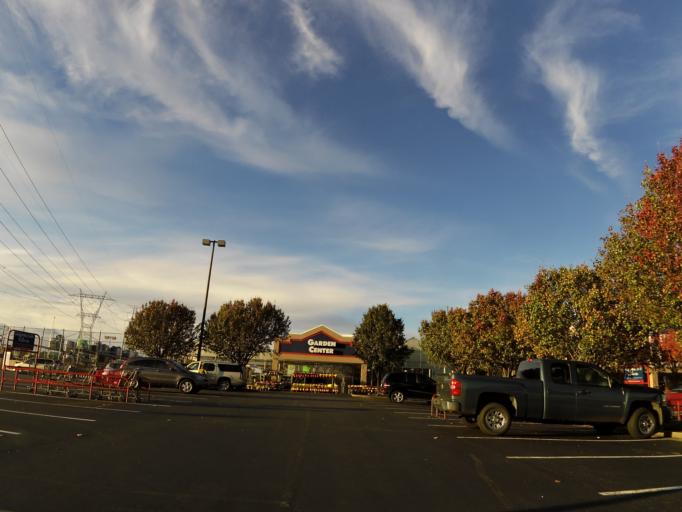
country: US
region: Tennessee
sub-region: Knox County
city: Farragut
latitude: 35.9176
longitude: -84.0829
